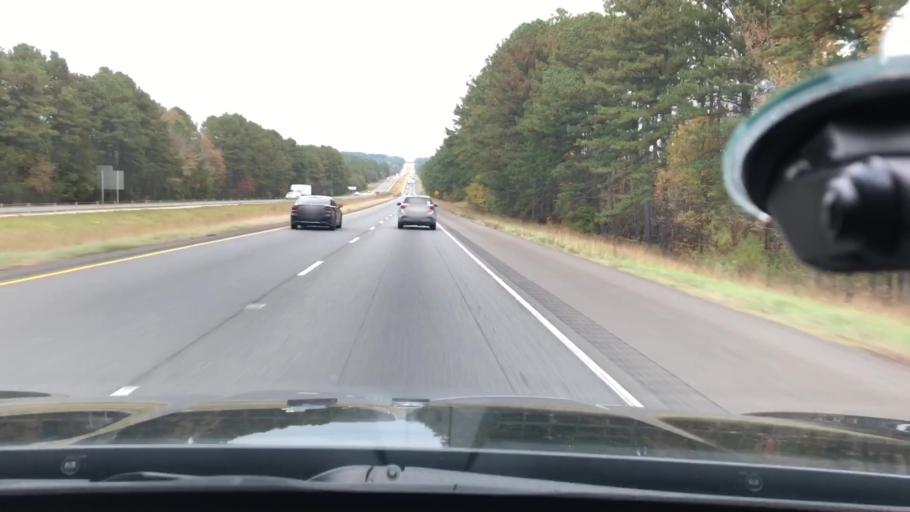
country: US
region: Arkansas
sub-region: Clark County
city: Arkadelphia
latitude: 34.2483
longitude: -92.9939
